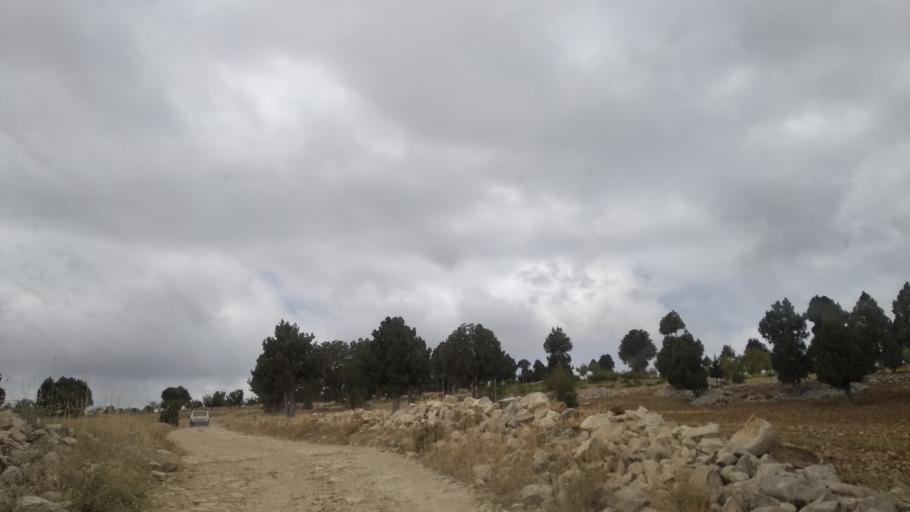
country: TR
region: Mersin
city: Sarikavak
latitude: 36.5650
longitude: 33.7684
